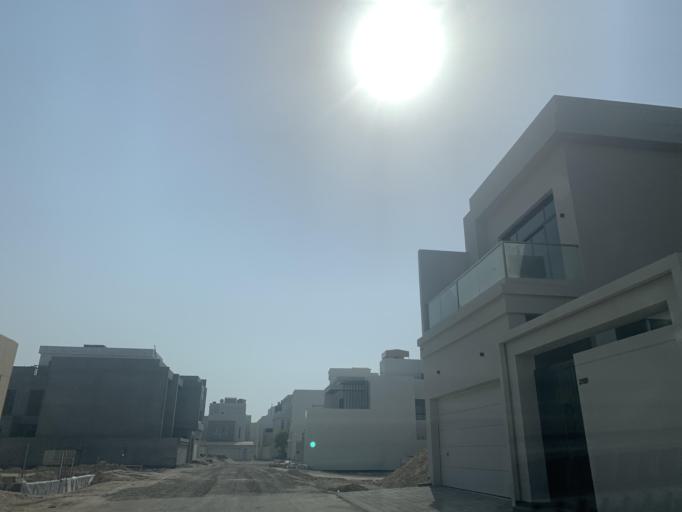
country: BH
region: Manama
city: Jidd Hafs
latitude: 26.2053
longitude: 50.4908
